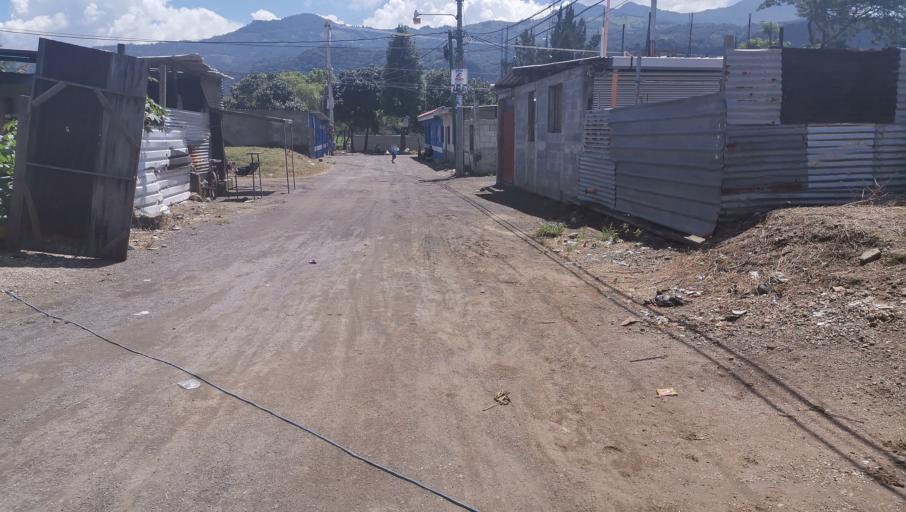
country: GT
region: Escuintla
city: San Vicente Pacaya
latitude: 14.4442
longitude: -90.6344
